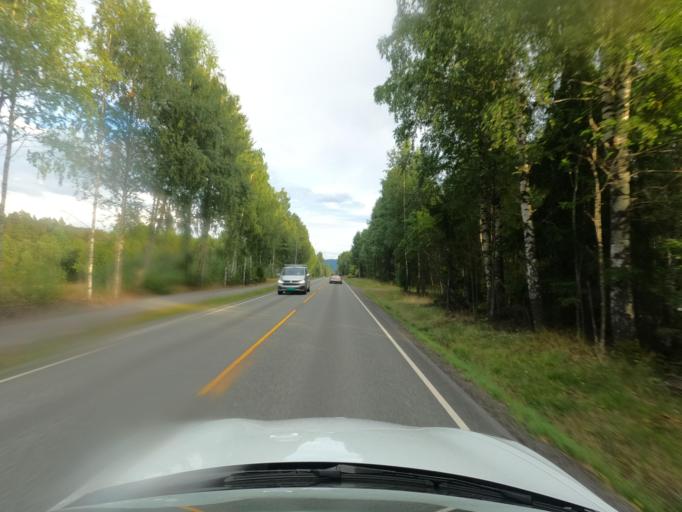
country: NO
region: Telemark
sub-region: Notodden
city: Notodden
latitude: 59.5892
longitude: 9.1552
